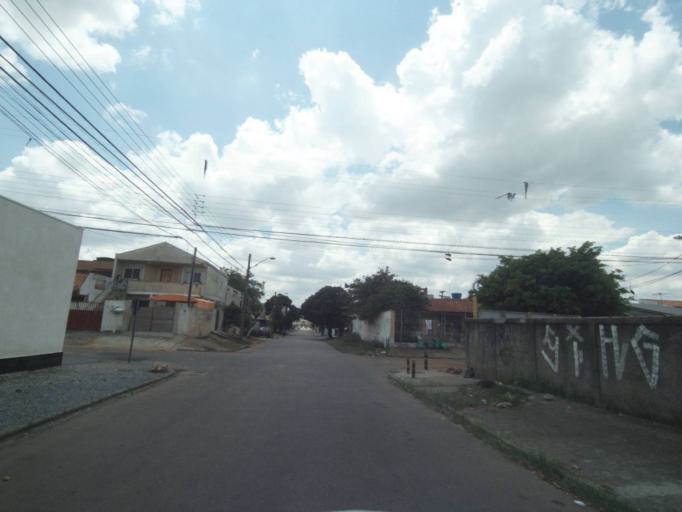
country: BR
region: Parana
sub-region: Sao Jose Dos Pinhais
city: Sao Jose dos Pinhais
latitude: -25.5423
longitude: -49.2686
